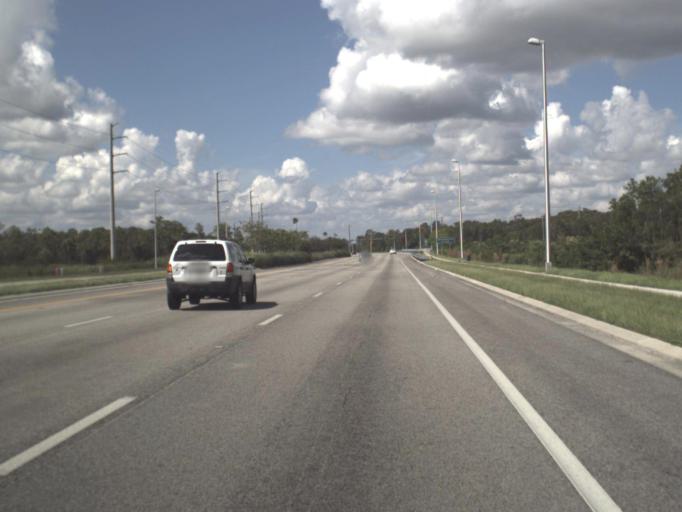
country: US
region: Florida
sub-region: Lee County
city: Gateway
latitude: 26.6234
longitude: -81.7731
